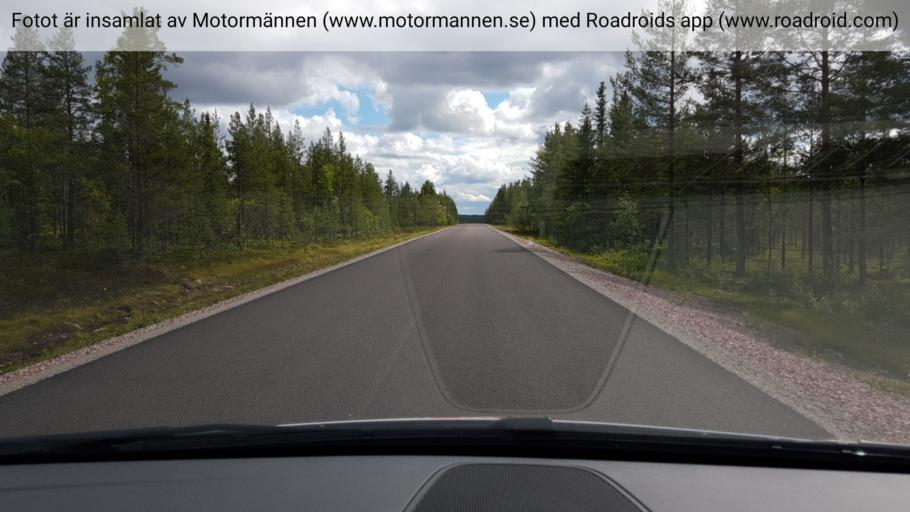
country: SE
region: Jaemtland
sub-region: Harjedalens Kommun
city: Sveg
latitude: 61.6651
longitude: 14.1736
